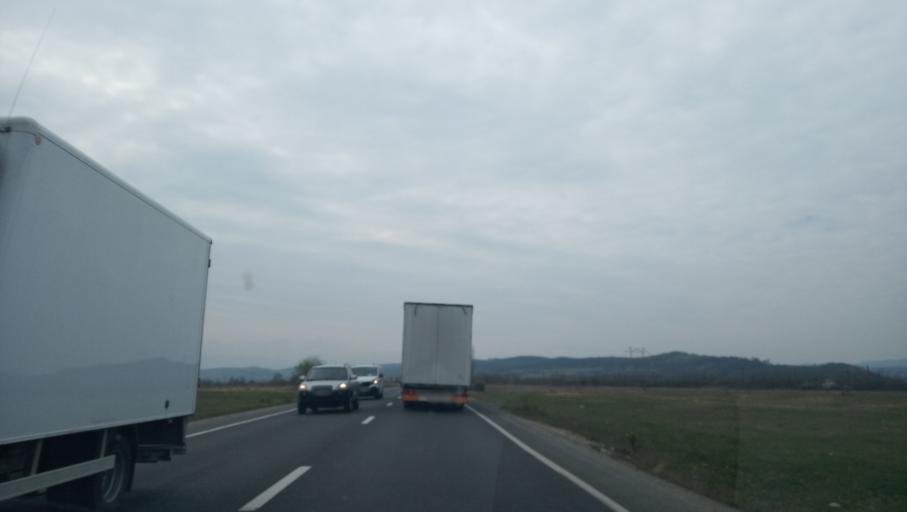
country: RO
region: Hunedoara
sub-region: Comuna Calan
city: Calan
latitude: 45.7091
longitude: 22.9906
